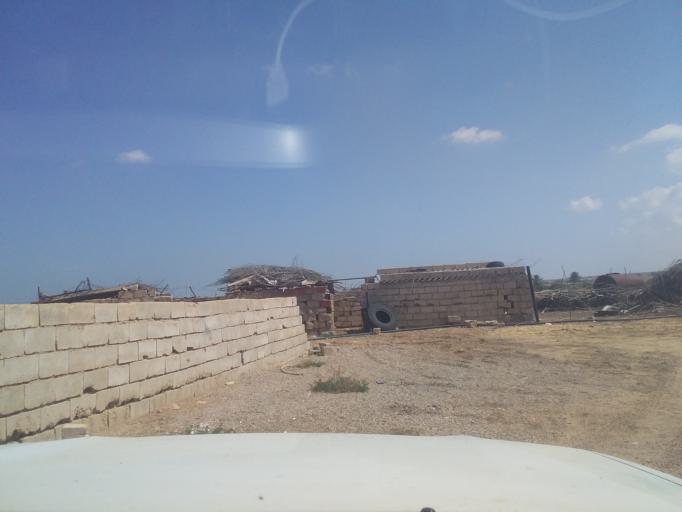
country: TN
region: Madanin
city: Medenine
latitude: 33.6114
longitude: 10.3128
